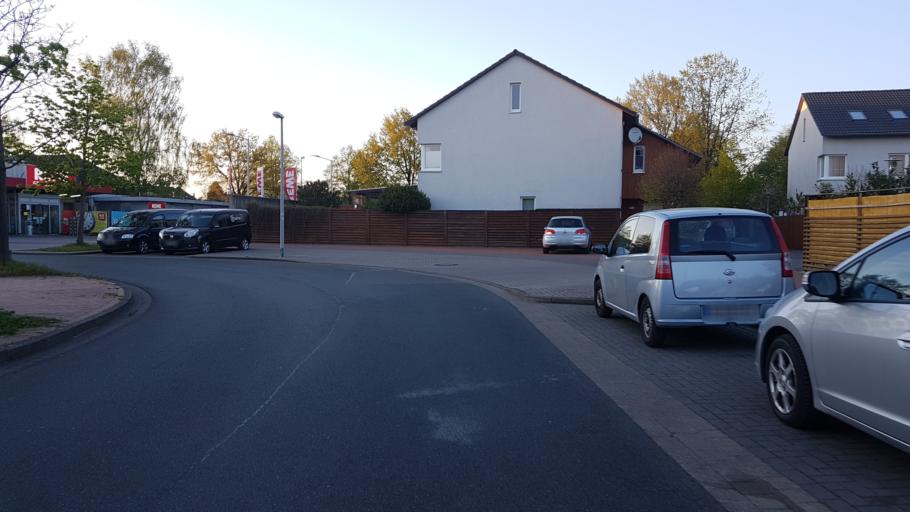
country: DE
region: Lower Saxony
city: Langenhagen
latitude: 52.4175
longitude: 9.7665
